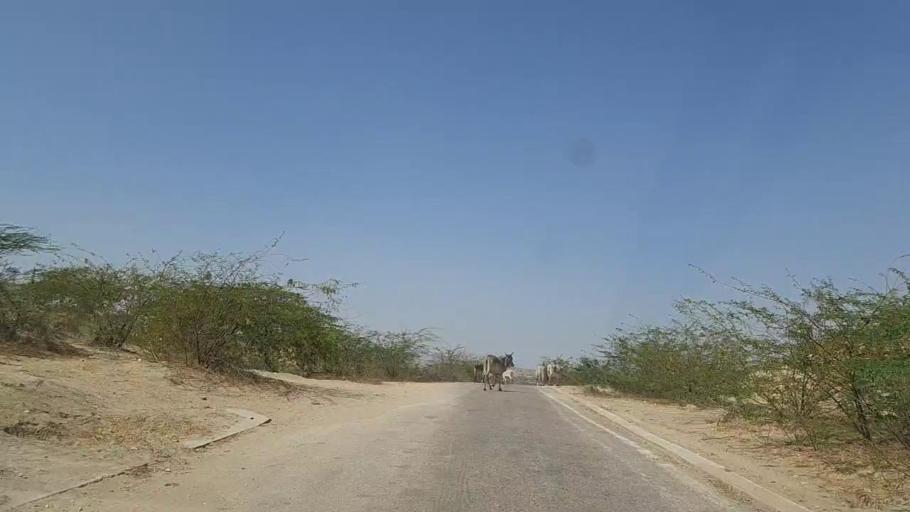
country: PK
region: Sindh
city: Naukot
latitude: 24.5888
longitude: 69.3168
